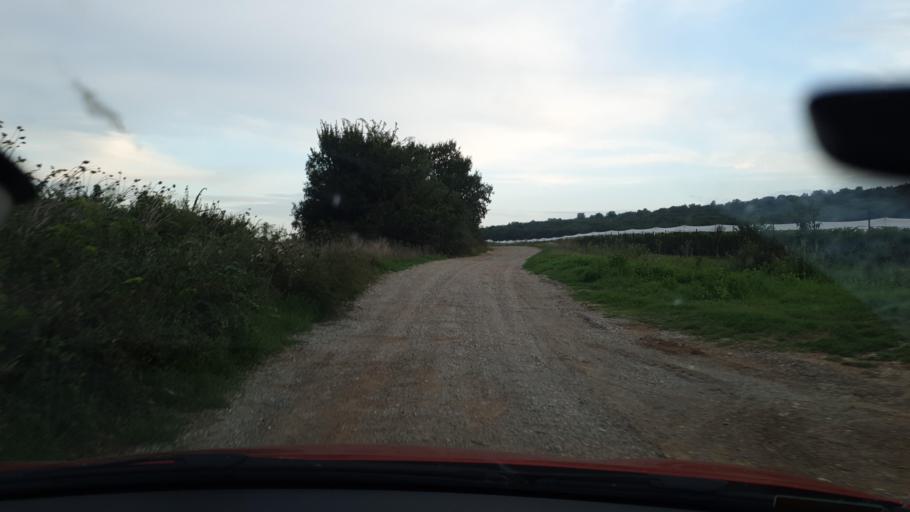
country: GR
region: Central Macedonia
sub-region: Nomos Kilkis
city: Kristoni
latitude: 40.9585
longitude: 22.8193
